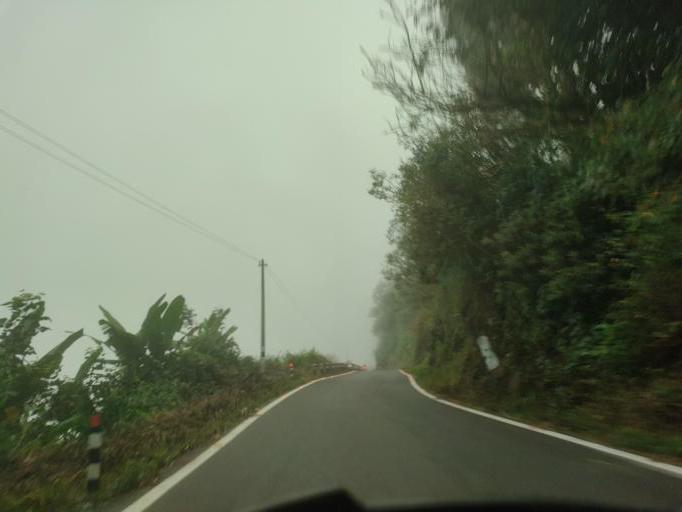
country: IN
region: Tamil Nadu
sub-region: Dindigul
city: Kodaikanal
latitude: 10.3314
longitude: 77.5641
